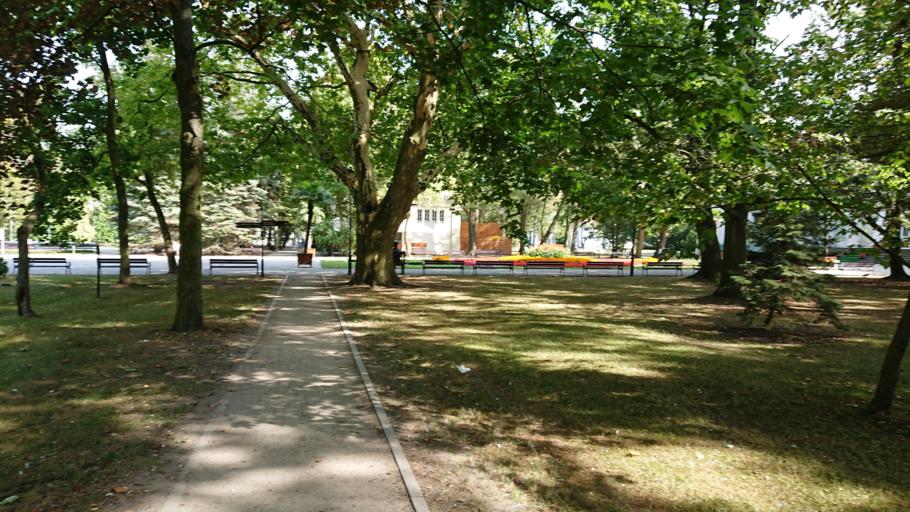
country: PL
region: Kujawsko-Pomorskie
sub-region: Powiat inowroclawski
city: Inowroclaw
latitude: 52.7938
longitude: 18.2396
